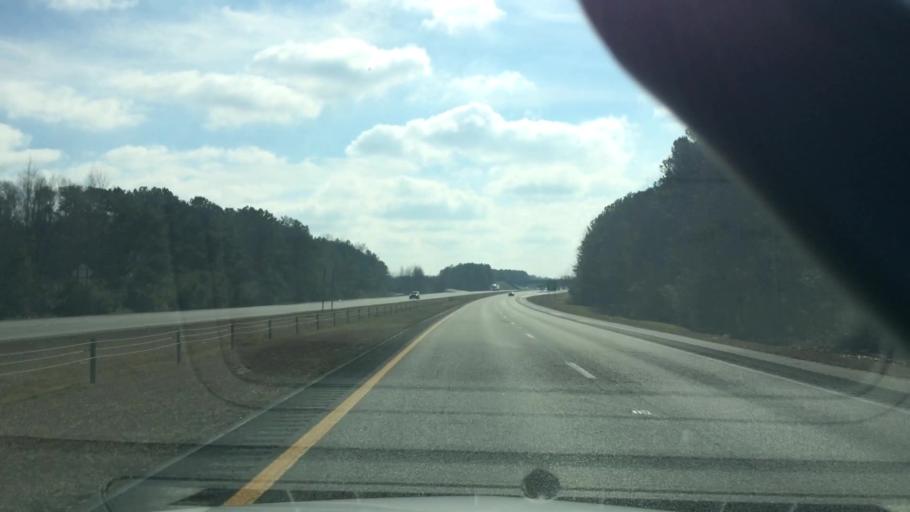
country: US
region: North Carolina
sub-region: Duplin County
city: Wallace
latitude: 34.6939
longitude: -77.9450
